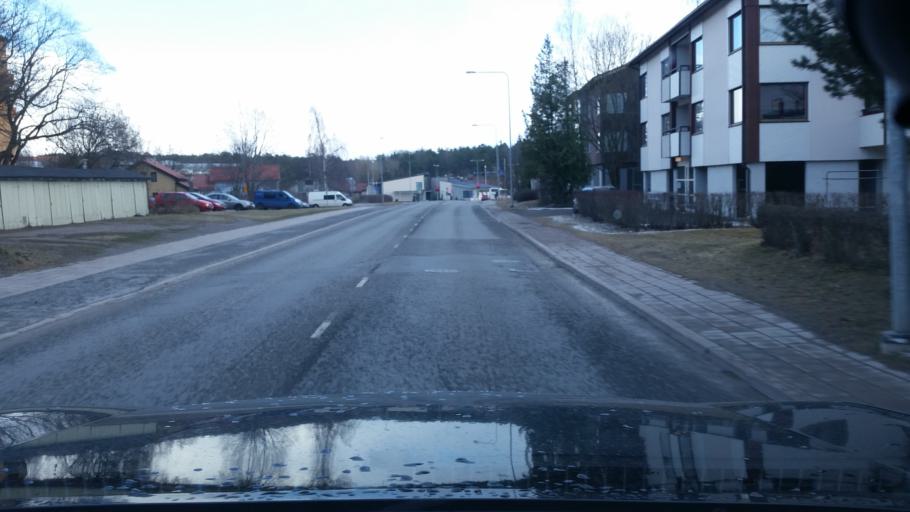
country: FI
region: Varsinais-Suomi
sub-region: Turku
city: Turku
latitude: 60.4339
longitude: 22.2649
